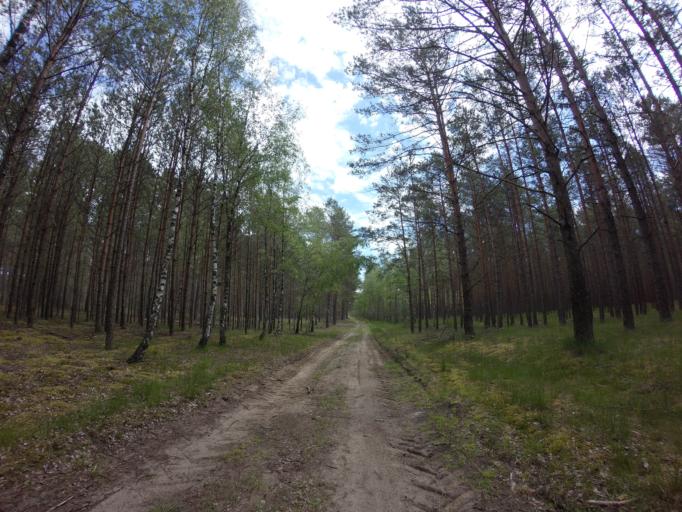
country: PL
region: West Pomeranian Voivodeship
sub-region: Powiat drawski
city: Kalisz Pomorski
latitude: 53.1733
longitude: 15.9636
